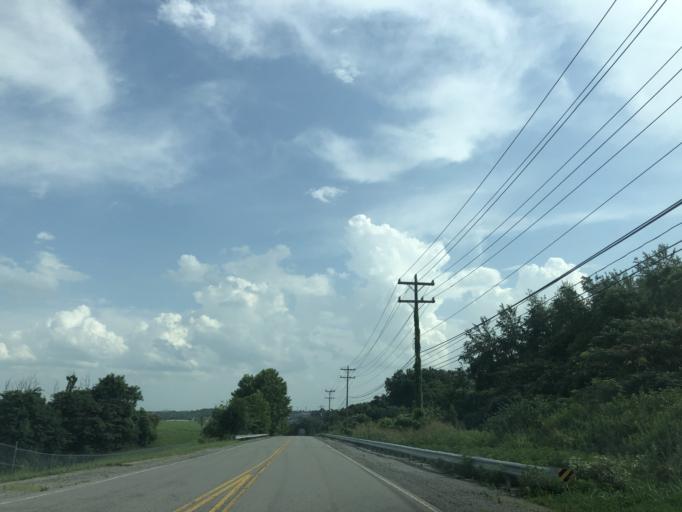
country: US
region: Tennessee
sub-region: Davidson County
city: Oak Hill
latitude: 36.1036
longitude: -86.6919
